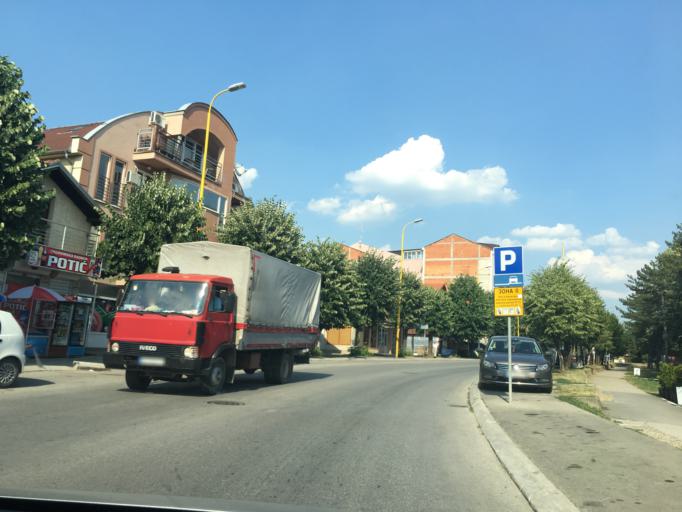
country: RS
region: Central Serbia
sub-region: Belgrade
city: Lazarevac
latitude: 44.3819
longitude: 20.2703
